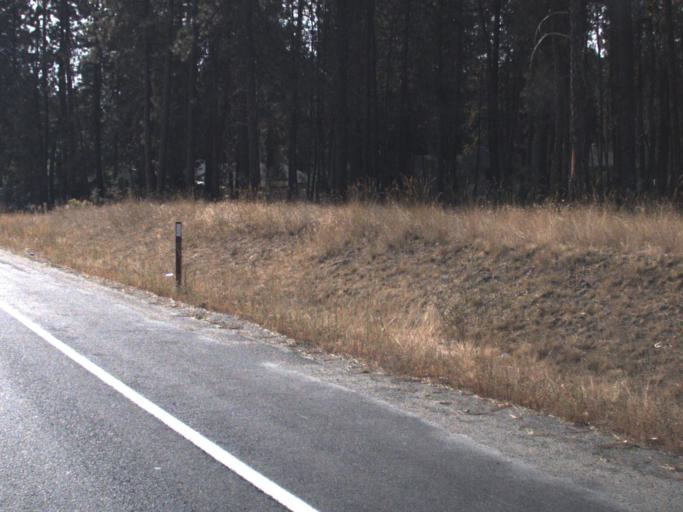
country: US
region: Washington
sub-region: Spokane County
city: Town and Country
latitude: 47.7513
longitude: -117.5112
